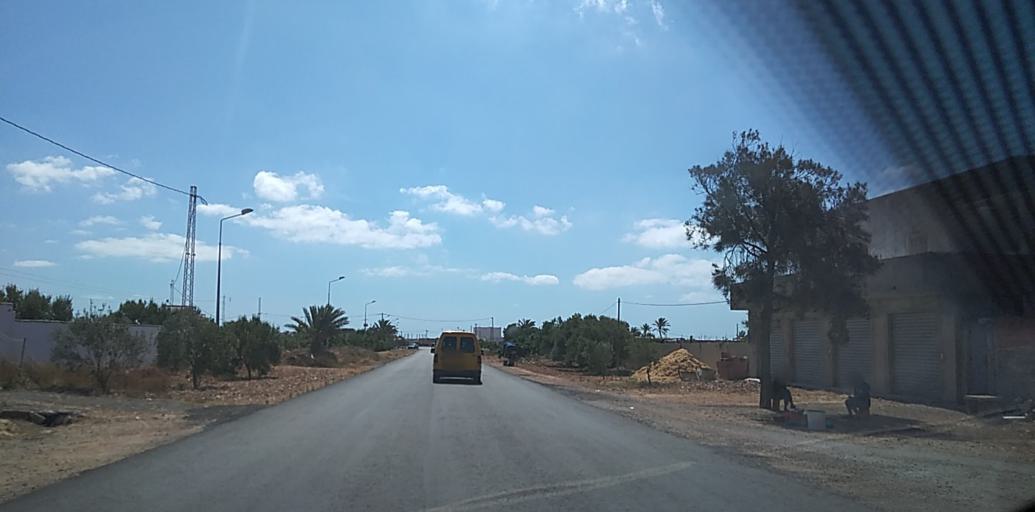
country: TN
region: Safaqis
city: Al Qarmadah
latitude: 34.6567
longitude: 11.0879
